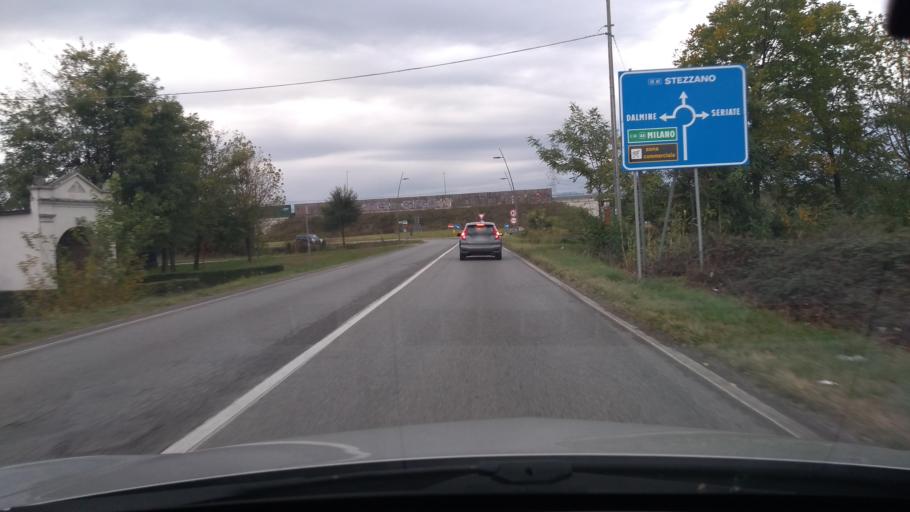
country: IT
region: Lombardy
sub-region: Provincia di Bergamo
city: Stezzano
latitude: 45.6360
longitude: 9.6445
